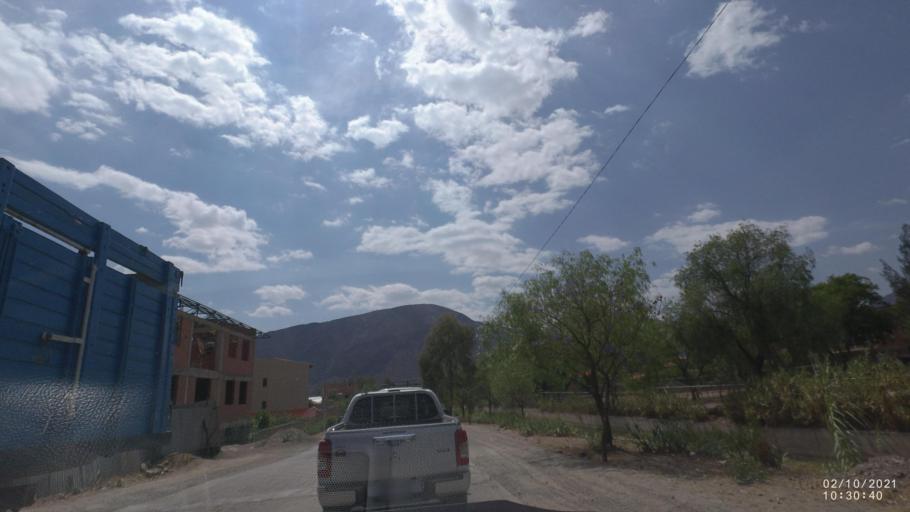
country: BO
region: Cochabamba
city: Capinota
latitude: -17.6963
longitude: -66.2645
